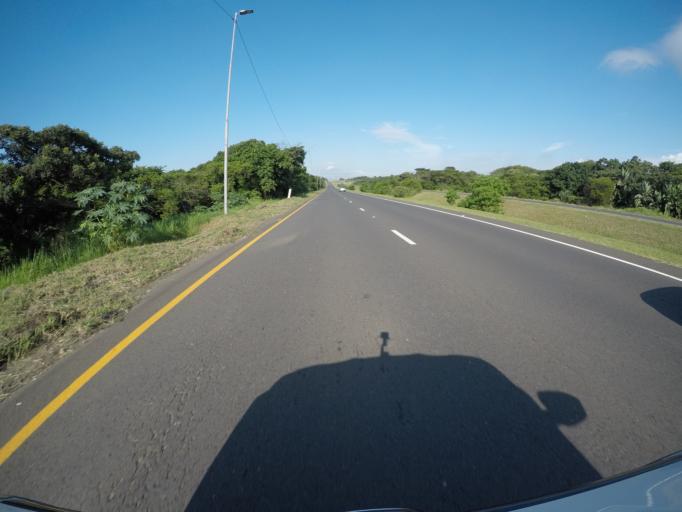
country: ZA
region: KwaZulu-Natal
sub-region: uThungulu District Municipality
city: Richards Bay
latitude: -28.7685
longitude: 32.0471
